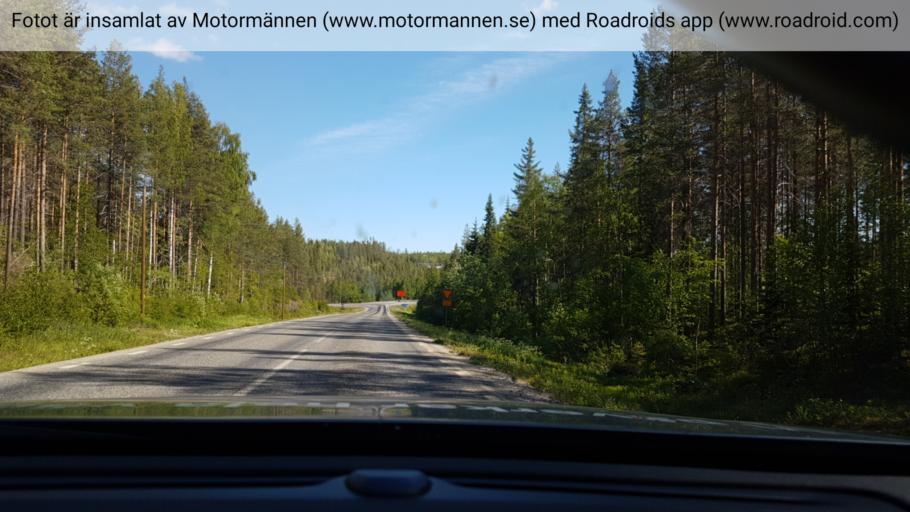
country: SE
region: Vaesterbotten
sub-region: Lycksele Kommun
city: Lycksele
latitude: 64.5775
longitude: 18.6477
